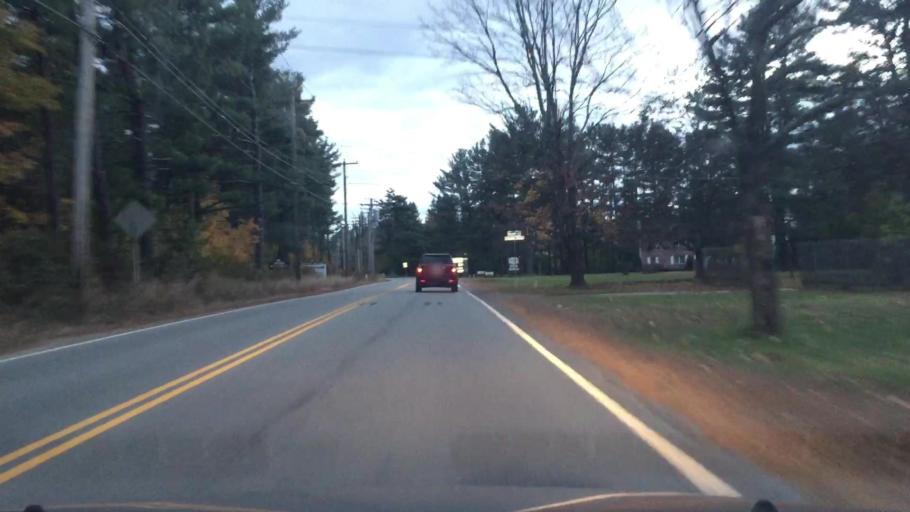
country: US
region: New Hampshire
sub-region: Cheshire County
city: Keene
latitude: 42.9108
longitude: -72.2652
